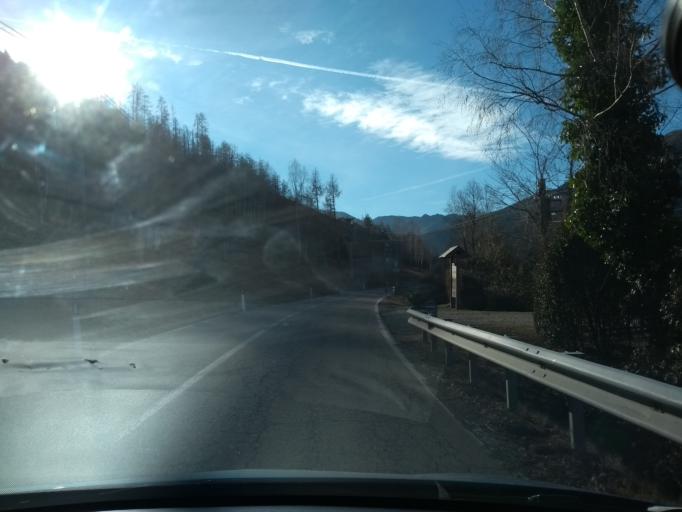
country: IT
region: Piedmont
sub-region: Provincia di Torino
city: La Villa
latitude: 45.2637
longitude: 7.4406
